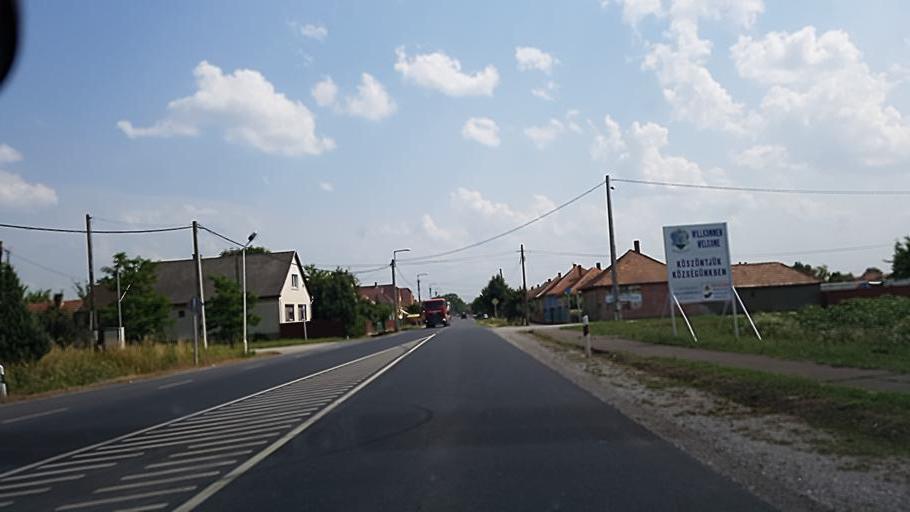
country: HU
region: Heves
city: Besenyotelek
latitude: 47.7097
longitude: 20.4249
